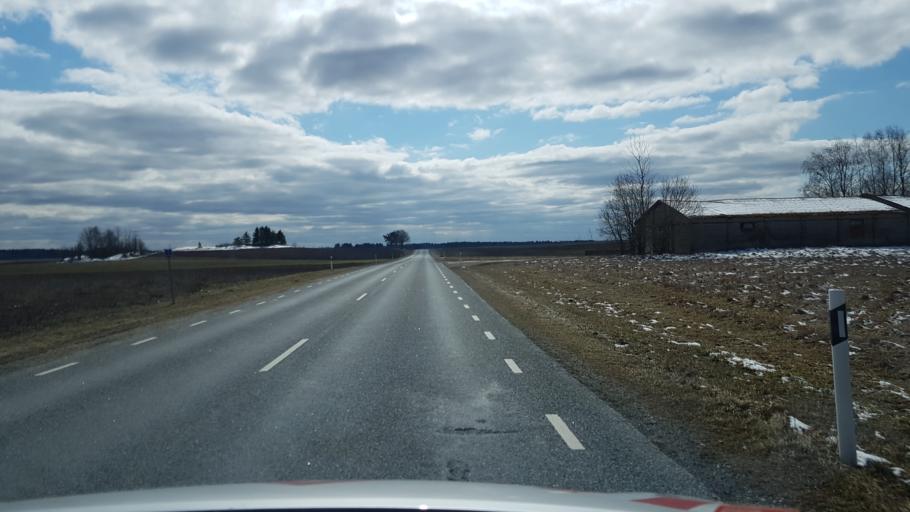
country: EE
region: Laeaene-Virumaa
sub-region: Tapa vald
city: Tapa
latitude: 59.3067
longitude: 26.0003
